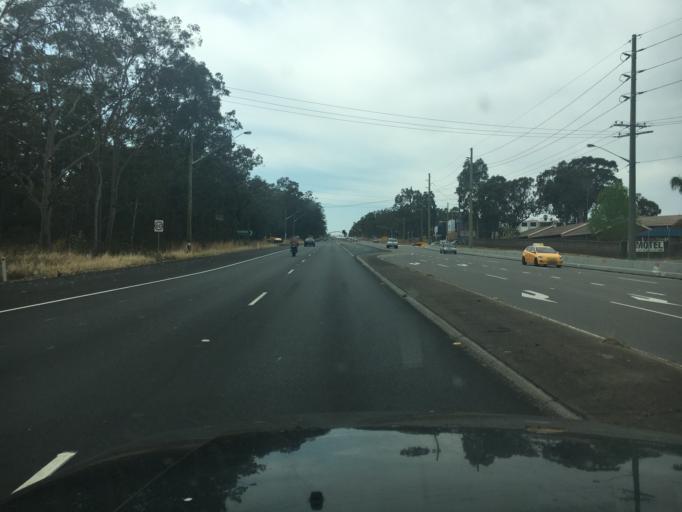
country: AU
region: New South Wales
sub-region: Maitland Municipality
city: East Maitland
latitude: -32.7625
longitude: 151.5963
